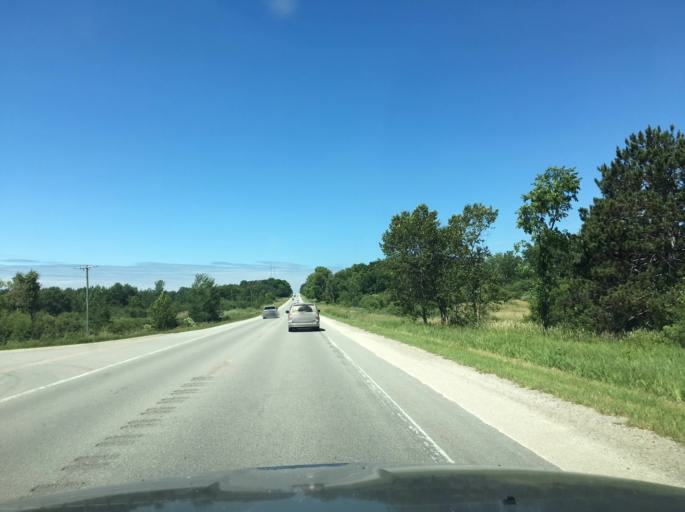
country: US
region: Michigan
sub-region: Osceola County
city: Reed City
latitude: 43.8877
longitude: -85.5721
